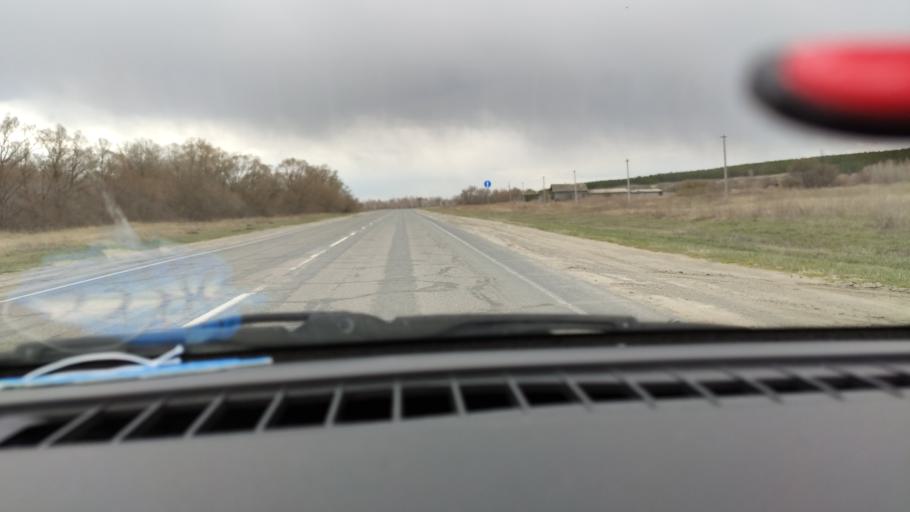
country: RU
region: Saratov
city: Sinodskoye
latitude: 52.0425
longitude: 46.7374
